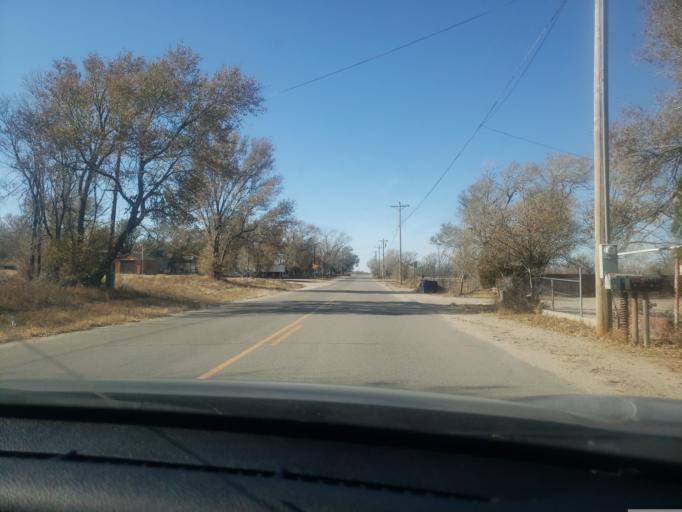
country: US
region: Kansas
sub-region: Finney County
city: Garden City
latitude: 37.9513
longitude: -100.8741
